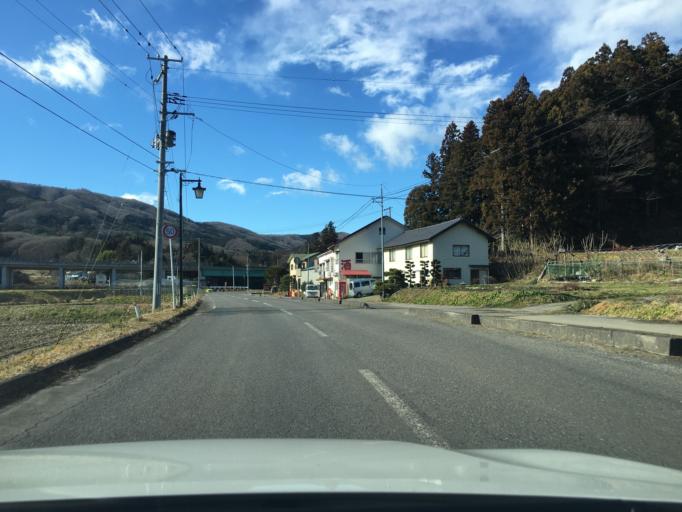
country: JP
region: Fukushima
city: Funehikimachi-funehiki
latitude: 37.3601
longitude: 140.6113
